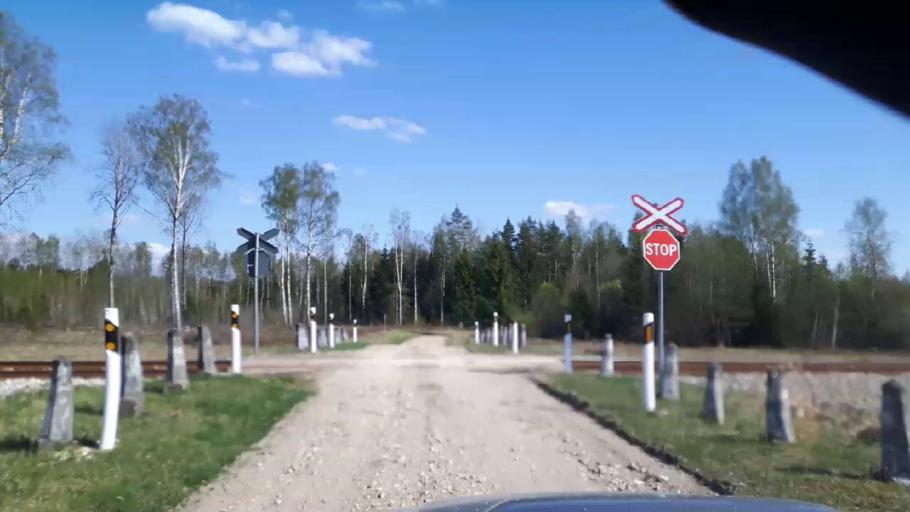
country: EE
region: Paernumaa
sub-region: Tootsi vald
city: Tootsi
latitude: 58.5405
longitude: 24.8129
